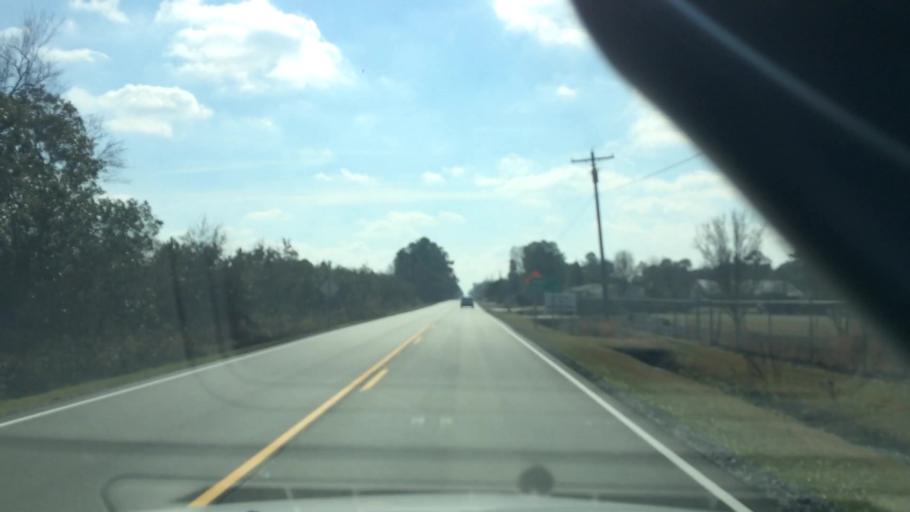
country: US
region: North Carolina
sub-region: Duplin County
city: Beulaville
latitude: 34.9957
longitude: -77.7563
